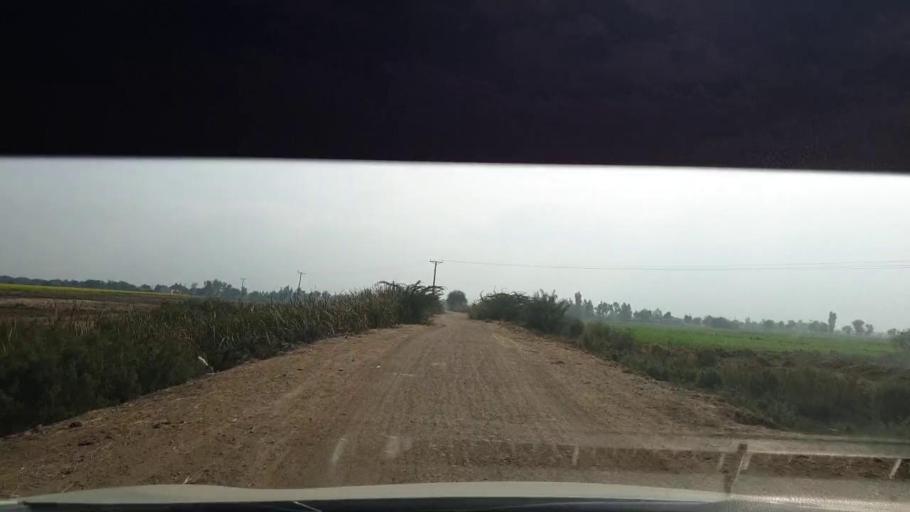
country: PK
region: Sindh
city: Berani
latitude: 25.7631
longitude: 68.8765
